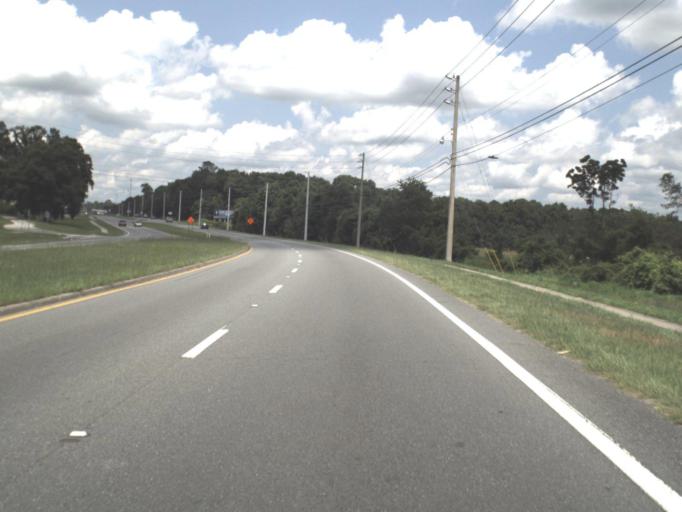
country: US
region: Florida
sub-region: Alachua County
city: Alachua
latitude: 29.7992
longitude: -82.5027
